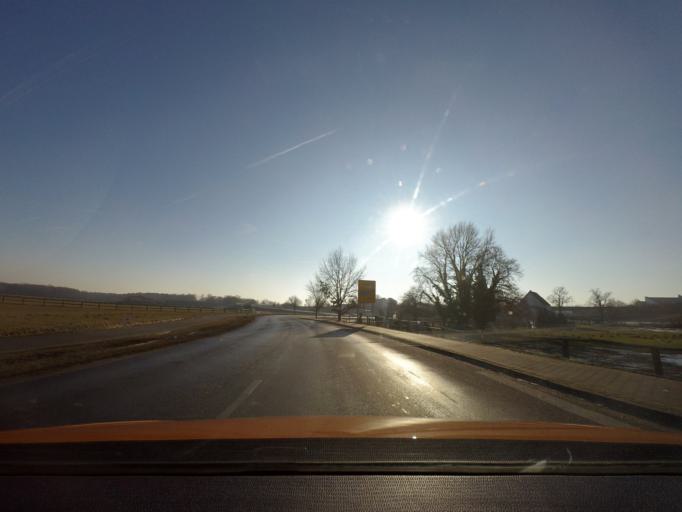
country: DE
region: Brandenburg
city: Falkensee
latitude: 52.5348
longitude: 13.0866
